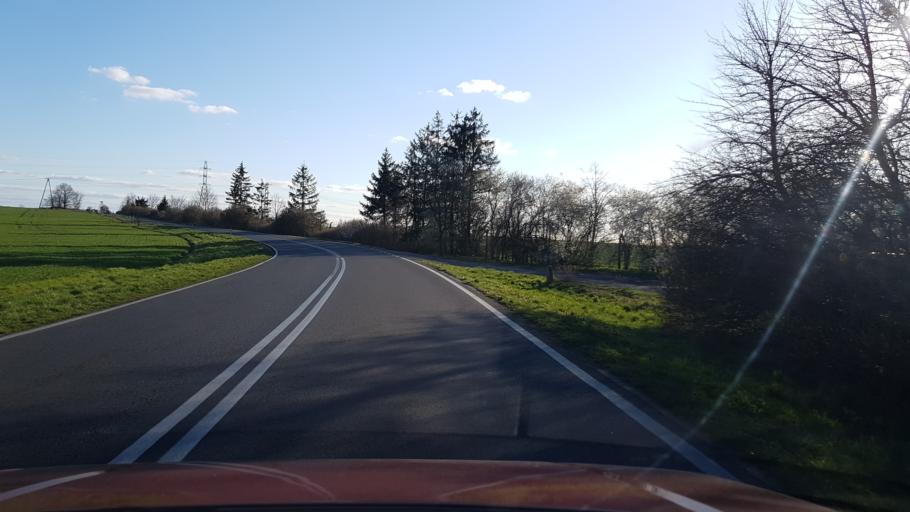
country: PL
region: West Pomeranian Voivodeship
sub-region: Powiat stargardzki
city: Stargard Szczecinski
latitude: 53.3599
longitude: 15.0619
